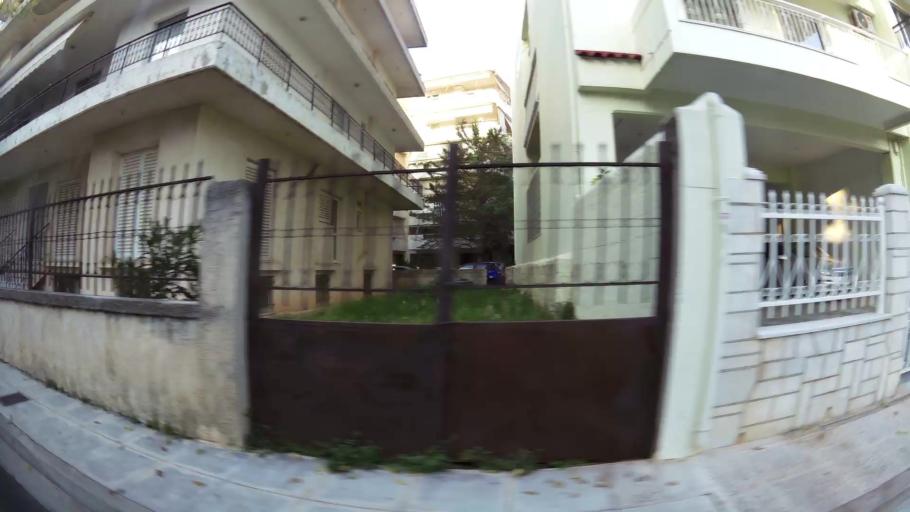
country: GR
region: Attica
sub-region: Nomarchia Athinas
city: Agia Paraskevi
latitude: 38.0177
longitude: 23.8201
